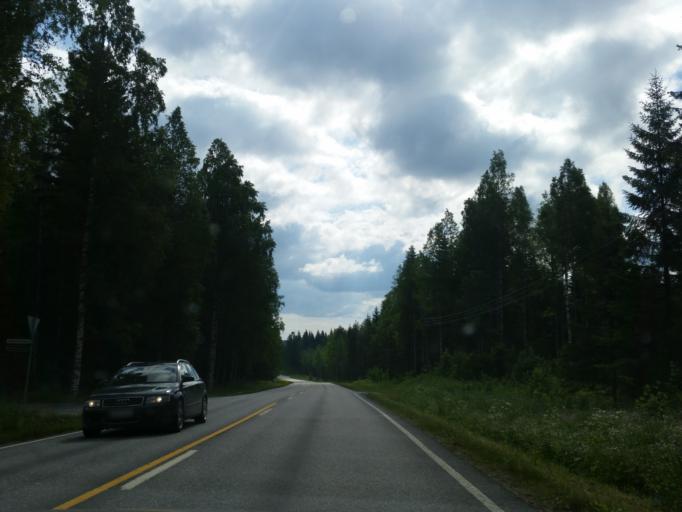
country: FI
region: Northern Savo
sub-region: Kuopio
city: Kuopio
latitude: 62.8458
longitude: 27.4028
